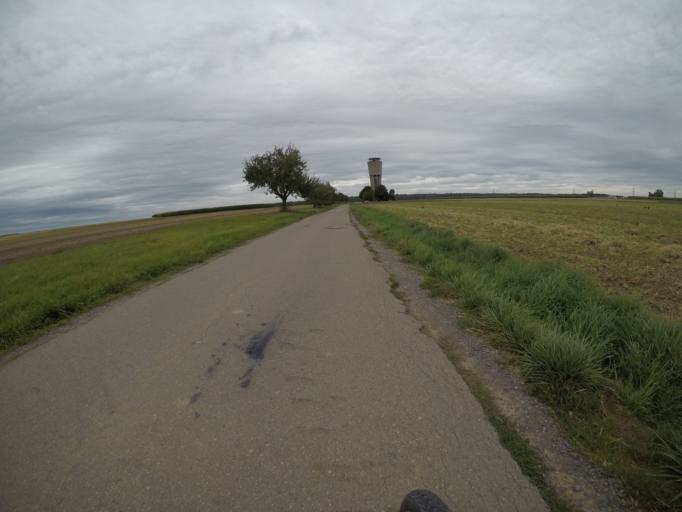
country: DE
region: Baden-Wuerttemberg
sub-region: Regierungsbezirk Stuttgart
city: Altdorf
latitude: 48.6387
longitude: 8.9933
